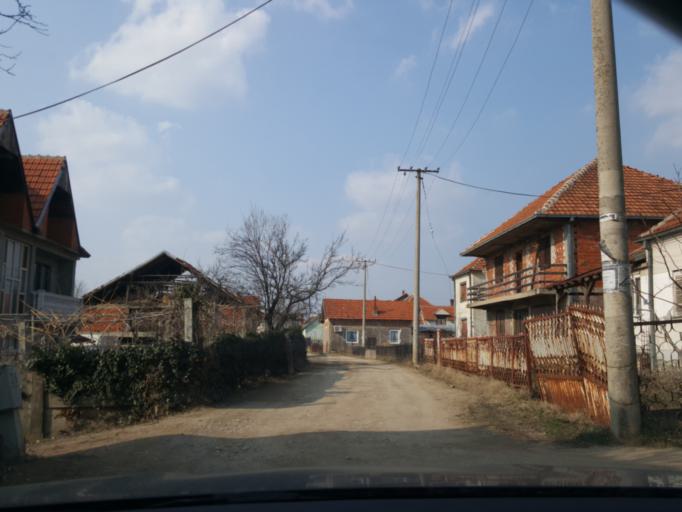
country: RS
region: Central Serbia
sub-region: Nisavski Okrug
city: Aleksinac
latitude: 43.5339
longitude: 21.7183
